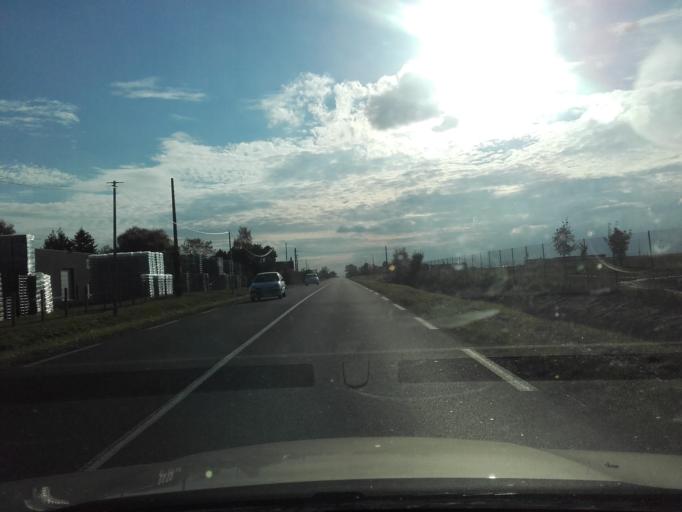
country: FR
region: Centre
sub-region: Departement d'Indre-et-Loire
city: Parcay-Meslay
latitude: 47.4710
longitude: 0.7529
